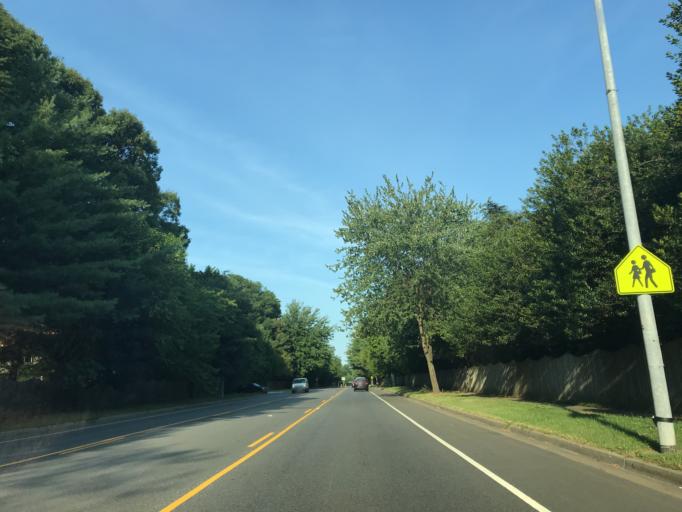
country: US
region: Maryland
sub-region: Anne Arundel County
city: South Gate
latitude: 39.1062
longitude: -76.6131
